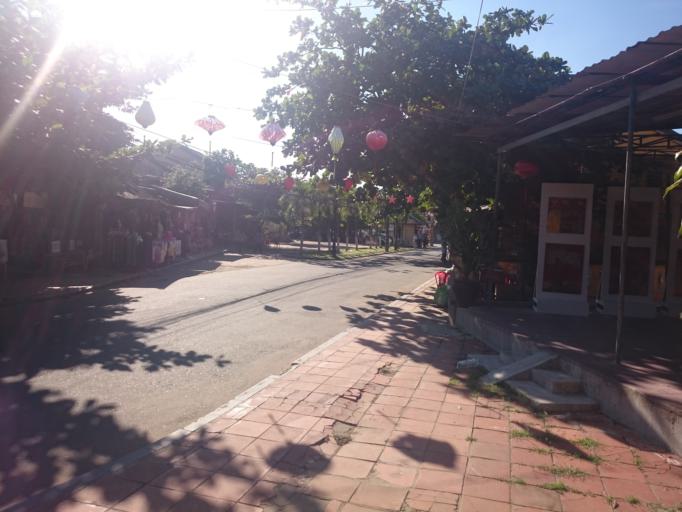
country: VN
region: Quang Nam
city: Hoi An
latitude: 15.8780
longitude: 108.3240
